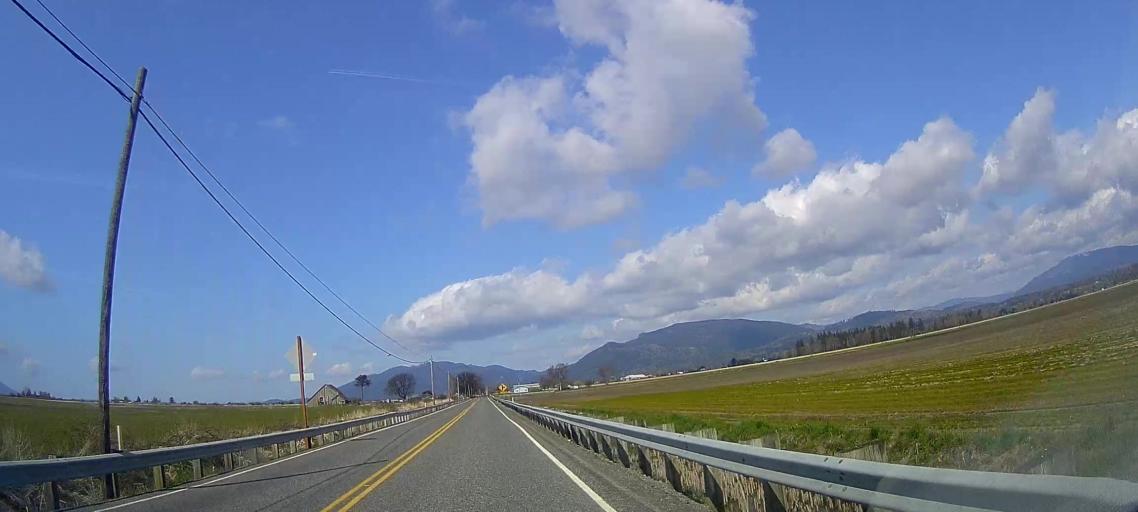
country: US
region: Washington
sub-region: Skagit County
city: Burlington
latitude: 48.5428
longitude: -122.4443
